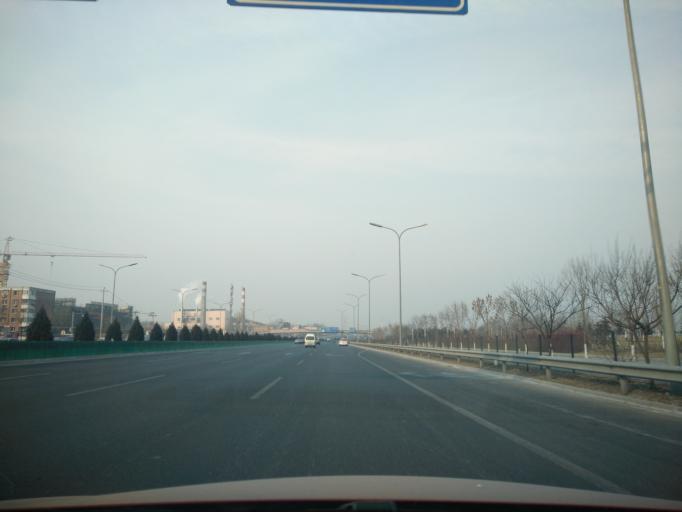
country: CN
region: Beijing
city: Jiugong
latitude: 39.7911
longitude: 116.4242
